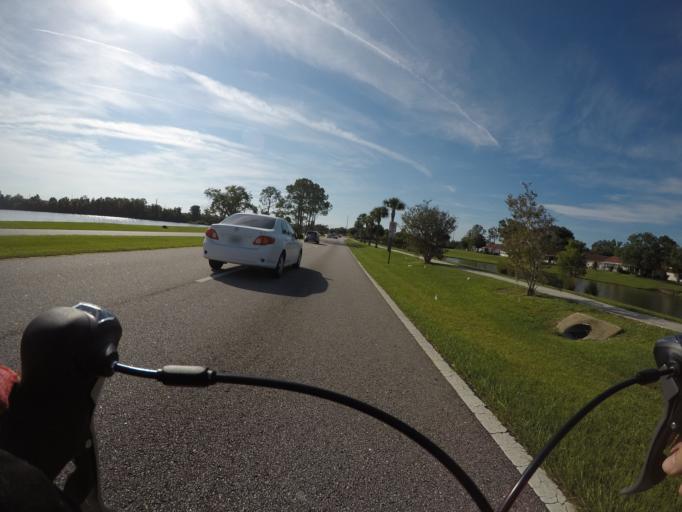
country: US
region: Florida
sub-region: Osceola County
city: Buenaventura Lakes
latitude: 28.3213
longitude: -81.3421
